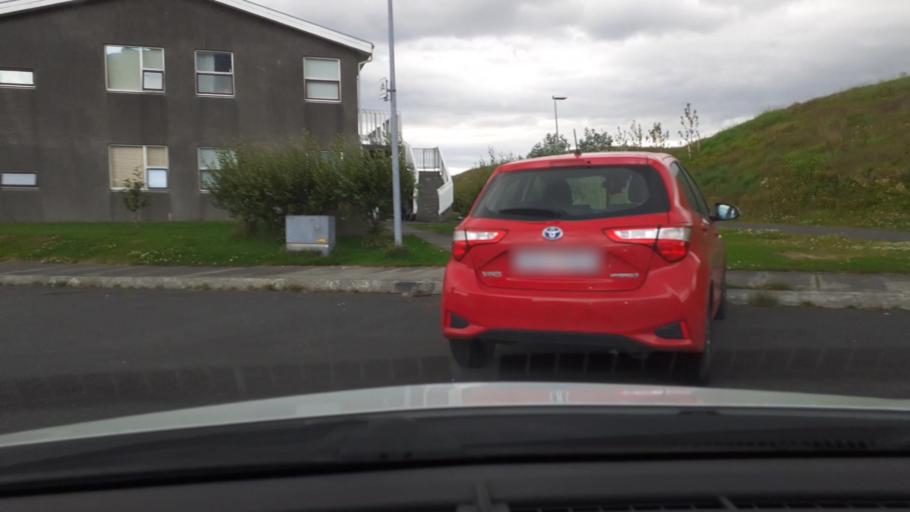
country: IS
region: Capital Region
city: Reykjavik
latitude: 64.2419
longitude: -21.8362
